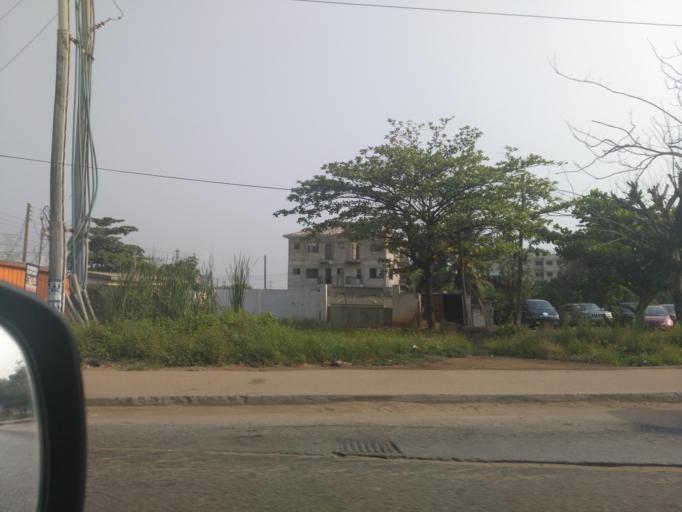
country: GH
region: Greater Accra
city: Accra
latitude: 5.6053
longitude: -0.2040
